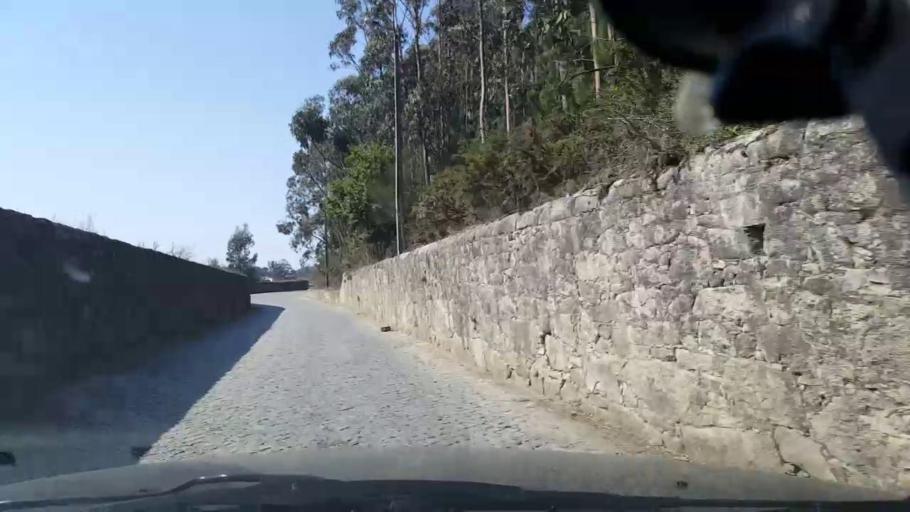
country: PT
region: Porto
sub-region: Vila do Conde
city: Arvore
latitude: 41.3825
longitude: -8.7076
